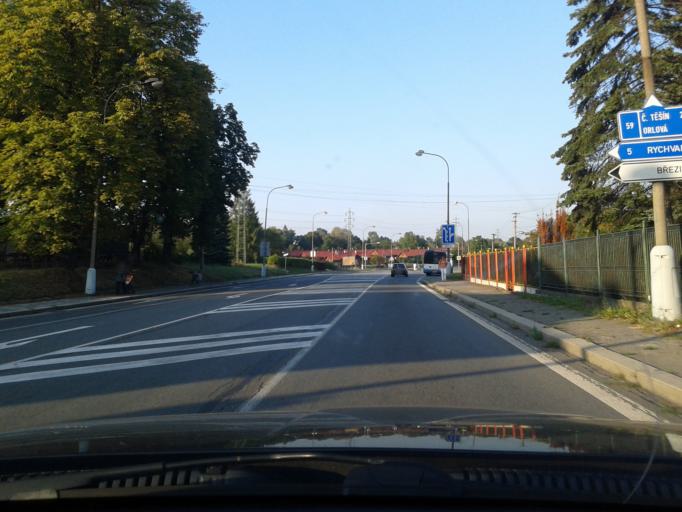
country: CZ
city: Petrvald
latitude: 49.8369
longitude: 18.4037
